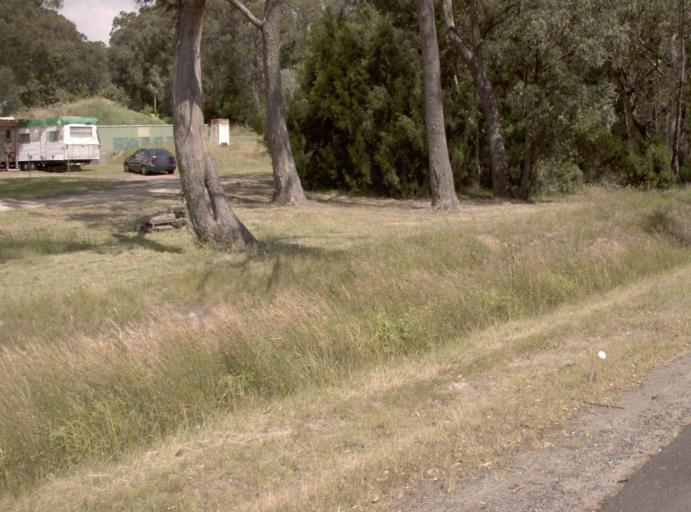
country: AU
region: Victoria
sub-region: Latrobe
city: Traralgon
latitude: -38.2975
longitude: 146.5380
